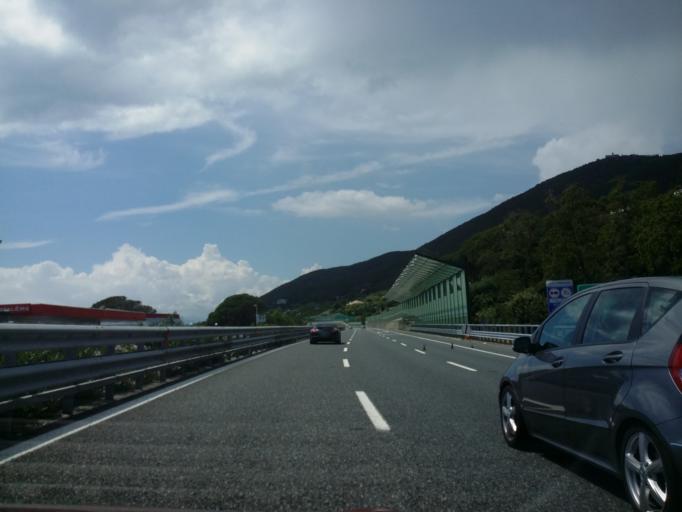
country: IT
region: Liguria
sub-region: Provincia di Savona
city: Varazze
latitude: 44.3695
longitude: 8.6118
